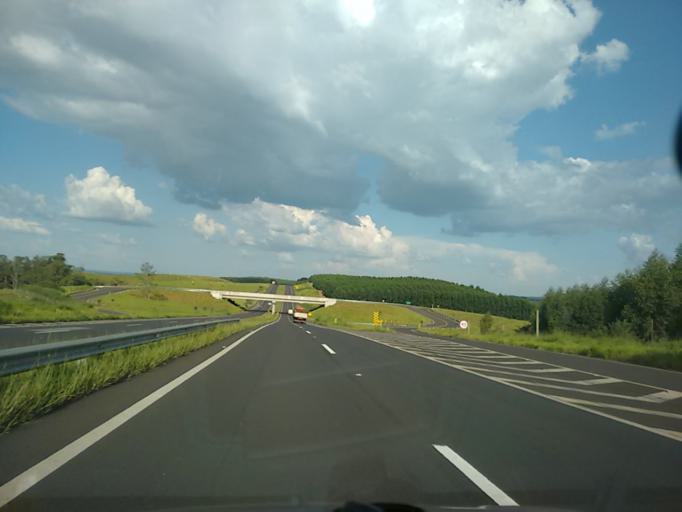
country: BR
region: Sao Paulo
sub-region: Duartina
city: Duartina
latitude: -22.3247
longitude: -49.4155
